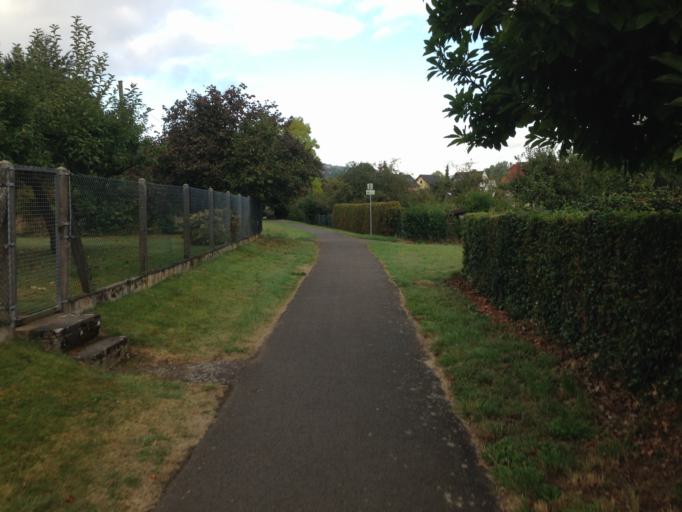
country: DE
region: Hesse
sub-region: Regierungsbezirk Giessen
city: Heuchelheim
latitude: 50.6175
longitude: 8.5952
